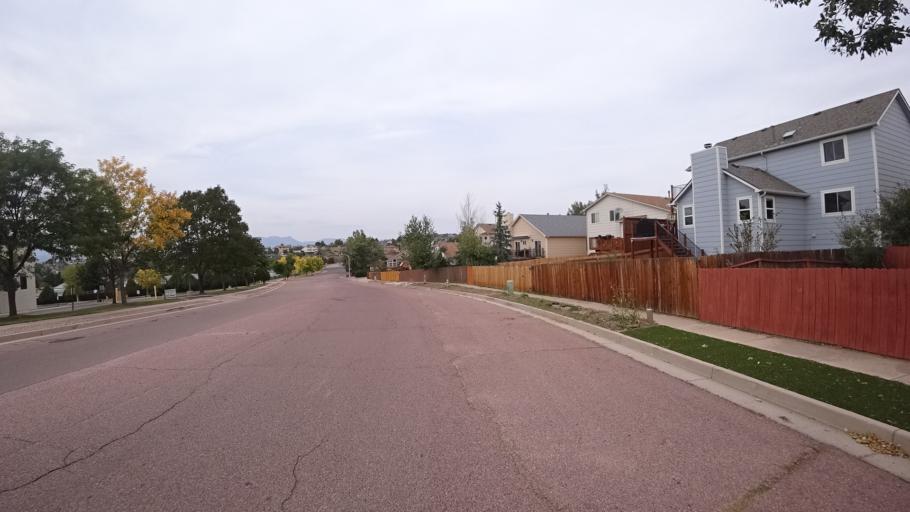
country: US
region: Colorado
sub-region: El Paso County
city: Cimarron Hills
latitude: 38.9071
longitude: -104.7346
